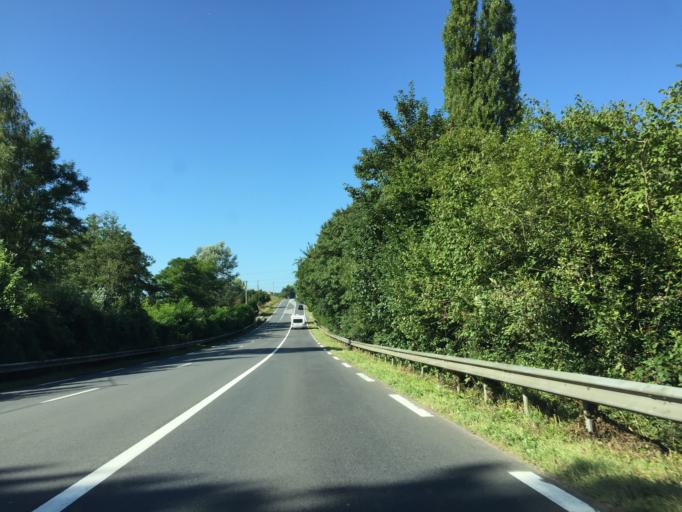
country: FR
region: Lower Normandy
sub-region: Departement du Calvados
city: Lisieux
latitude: 49.2027
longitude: 0.2268
